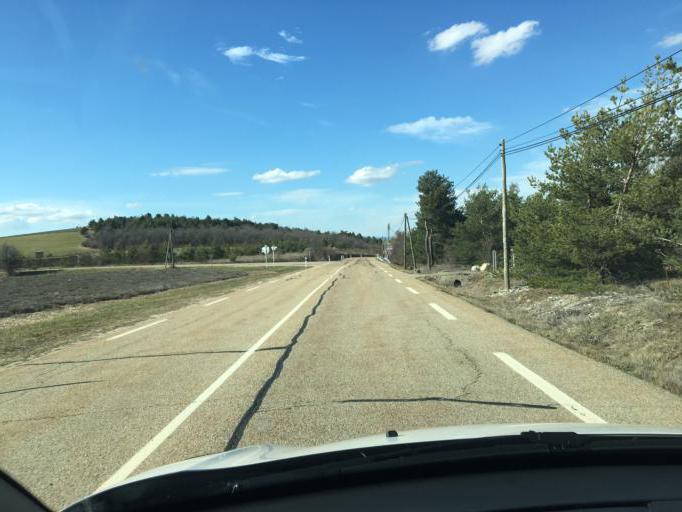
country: FR
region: Provence-Alpes-Cote d'Azur
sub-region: Departement du Vaucluse
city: Sault
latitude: 44.0277
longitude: 5.4674
